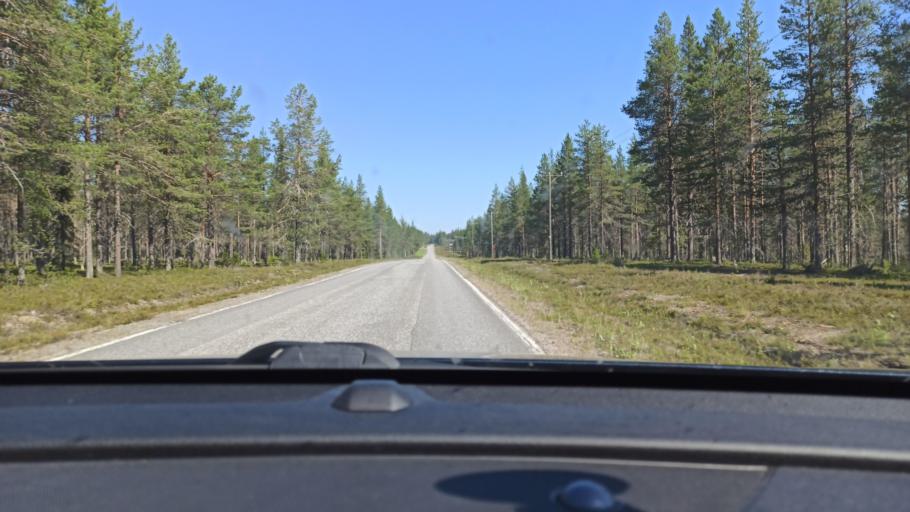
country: FI
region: Lapland
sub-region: Tunturi-Lappi
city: Kolari
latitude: 67.6491
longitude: 24.1614
